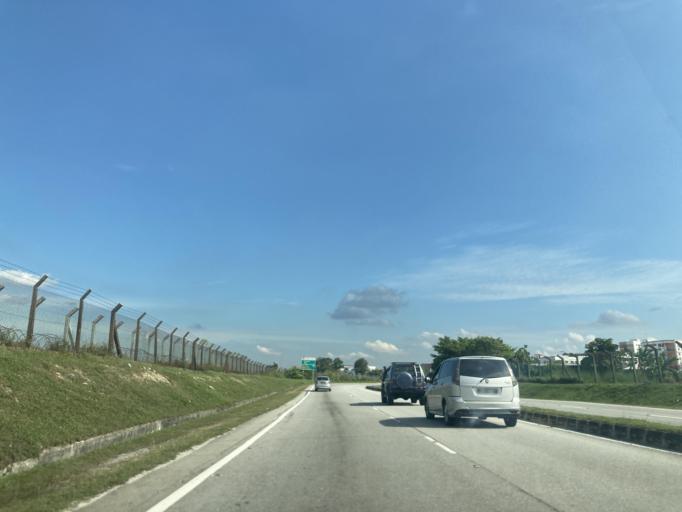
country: MY
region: Selangor
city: Kampung Baru Subang
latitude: 3.1476
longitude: 101.5390
